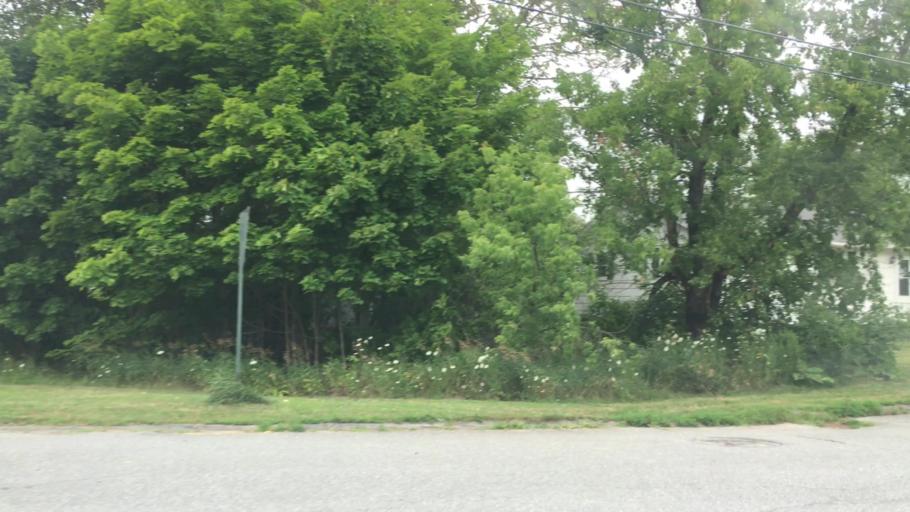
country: US
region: Maine
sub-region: Penobscot County
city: Brewer
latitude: 44.7734
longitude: -68.7694
